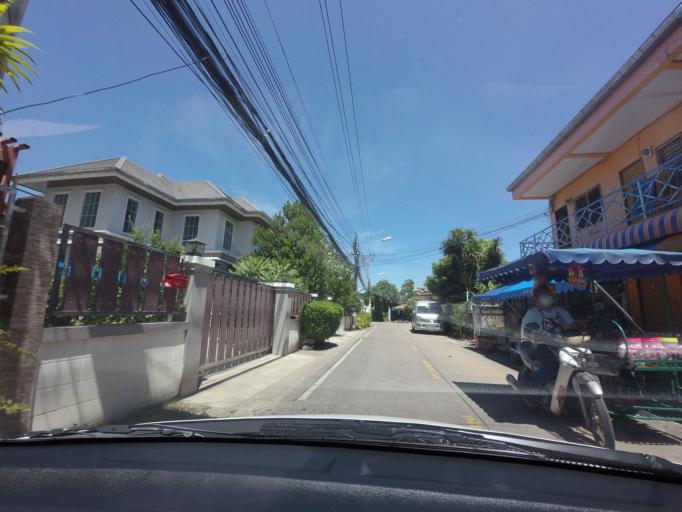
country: TH
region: Chon Buri
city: Phatthaya
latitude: 12.9543
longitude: 100.8952
